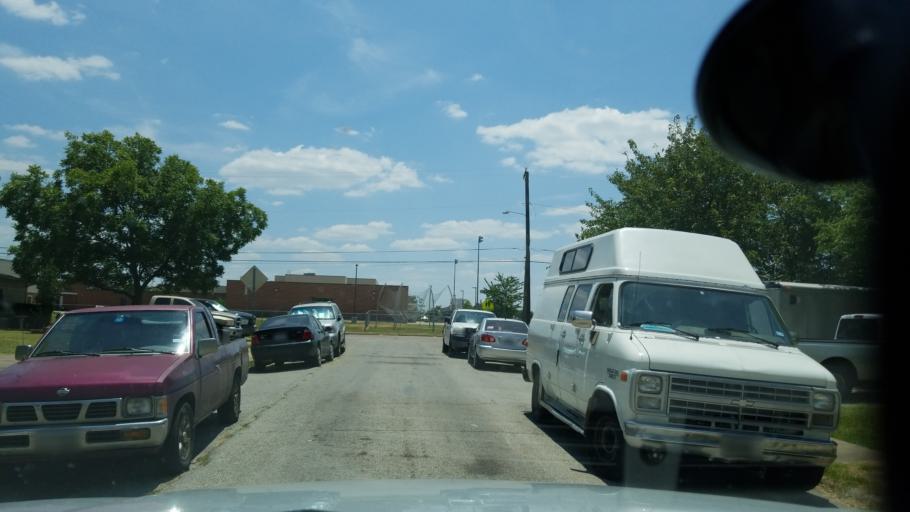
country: US
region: Texas
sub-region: Dallas County
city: Grand Prairie
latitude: 32.7535
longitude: -96.9648
